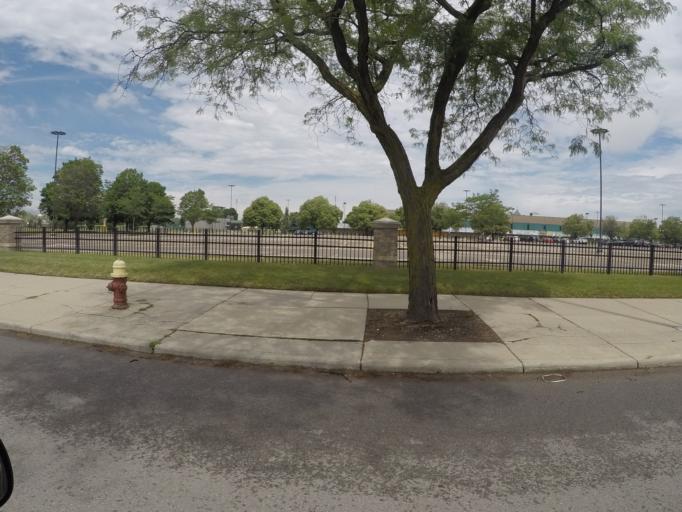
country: US
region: Michigan
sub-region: Wayne County
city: Detroit
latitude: 42.3533
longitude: -83.0759
